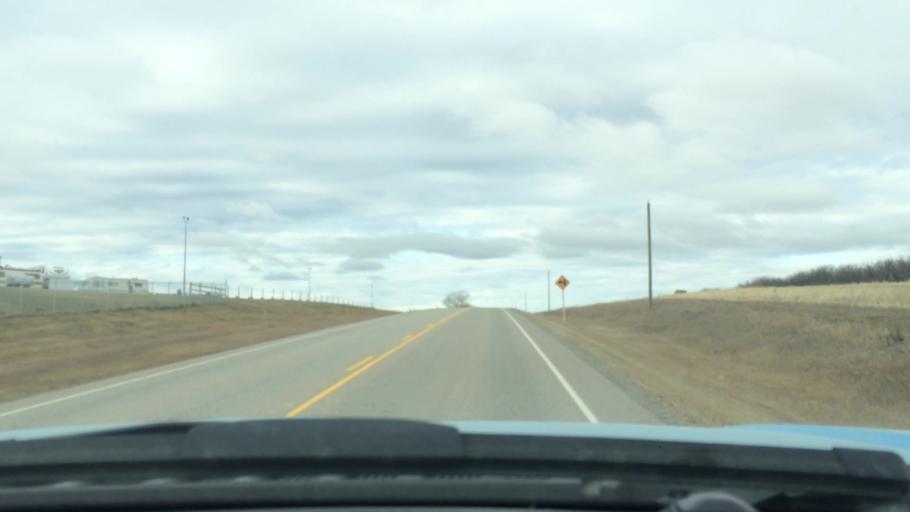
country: CA
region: Alberta
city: Airdrie
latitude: 51.2126
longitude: -114.0502
